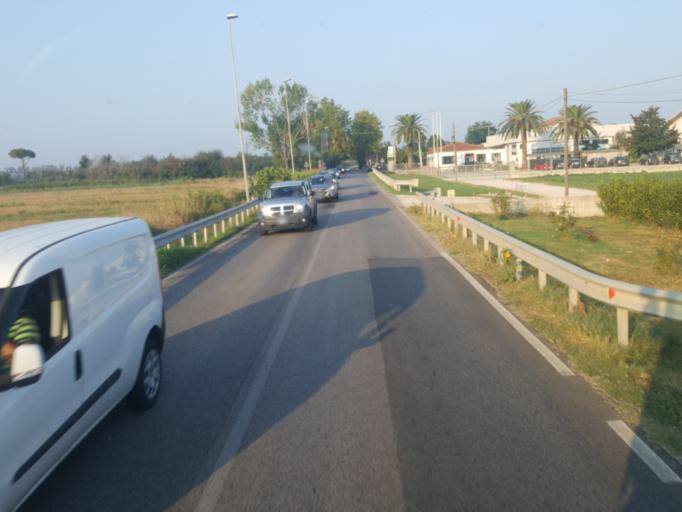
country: IT
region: Latium
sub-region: Provincia di Latina
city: Borgo San Michele
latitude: 41.4646
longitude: 13.0065
